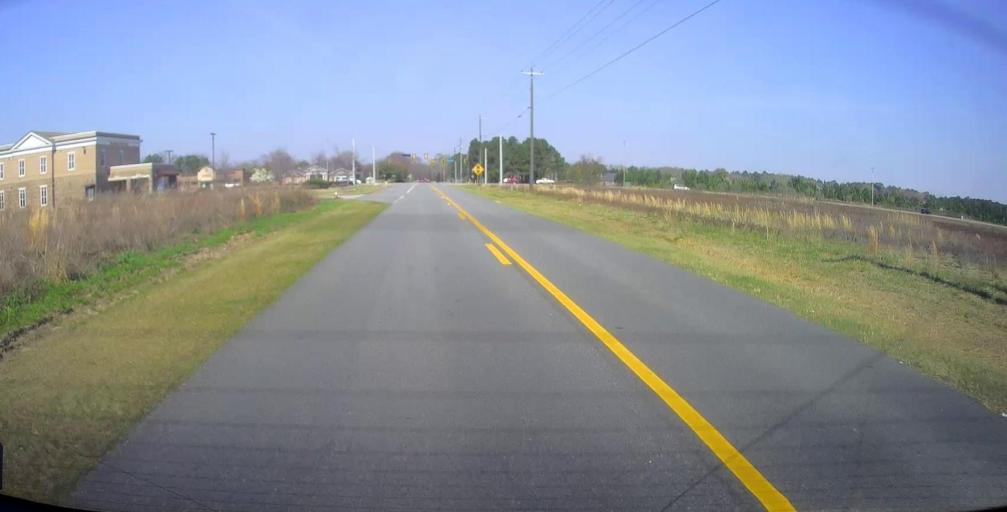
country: US
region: Georgia
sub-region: Houston County
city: Centerville
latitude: 32.5801
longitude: -83.7007
